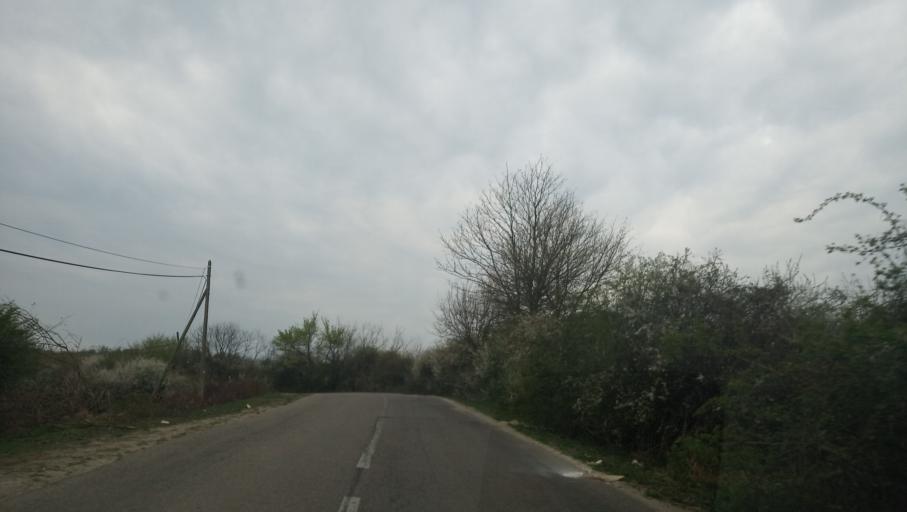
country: RO
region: Bihor
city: Hidiselu de Sus
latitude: 46.9238
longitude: 22.0513
